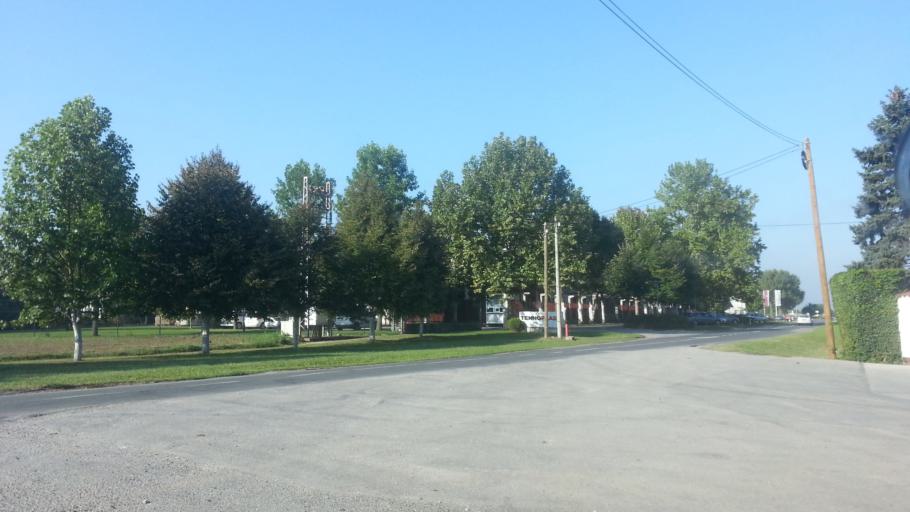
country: RS
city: Stari Banovci
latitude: 44.9863
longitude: 20.2643
